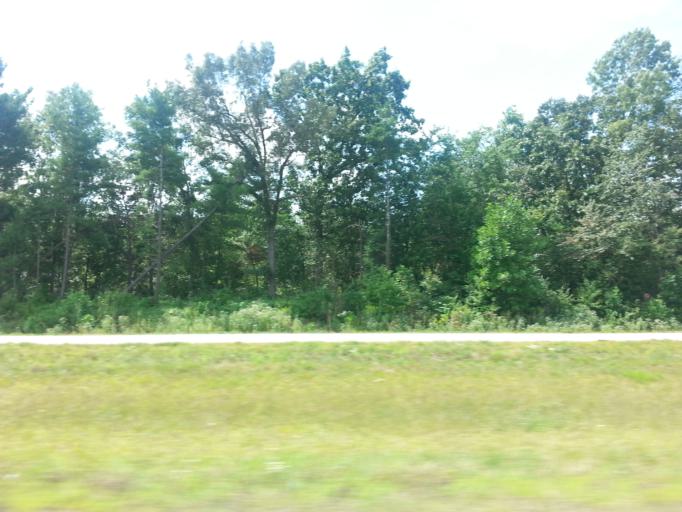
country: US
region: Tennessee
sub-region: Cumberland County
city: Crossville
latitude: 35.9881
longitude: -85.0215
